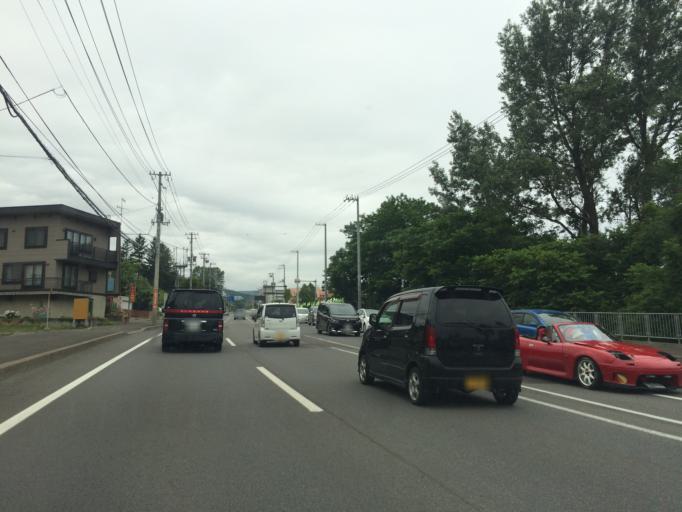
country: JP
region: Hokkaido
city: Otaru
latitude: 43.1388
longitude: 141.1630
